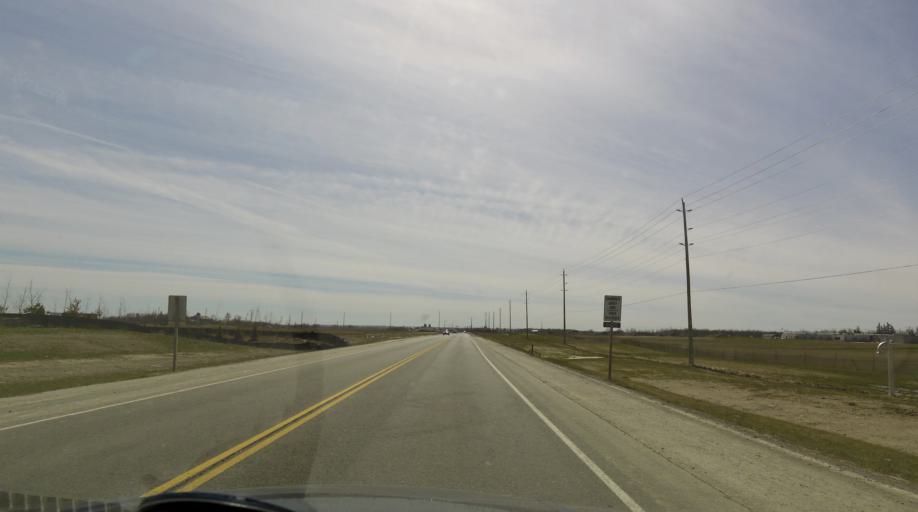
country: CA
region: Ontario
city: Brampton
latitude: 43.6984
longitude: -79.8637
